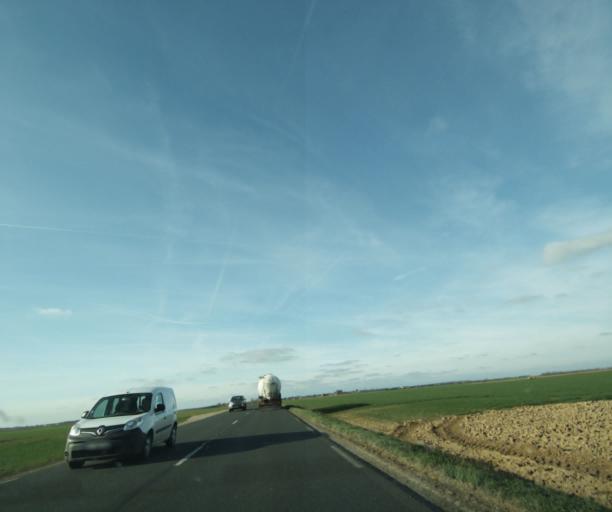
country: FR
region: Ile-de-France
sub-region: Departement des Yvelines
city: Ablis
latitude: 48.4976
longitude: 1.8415
